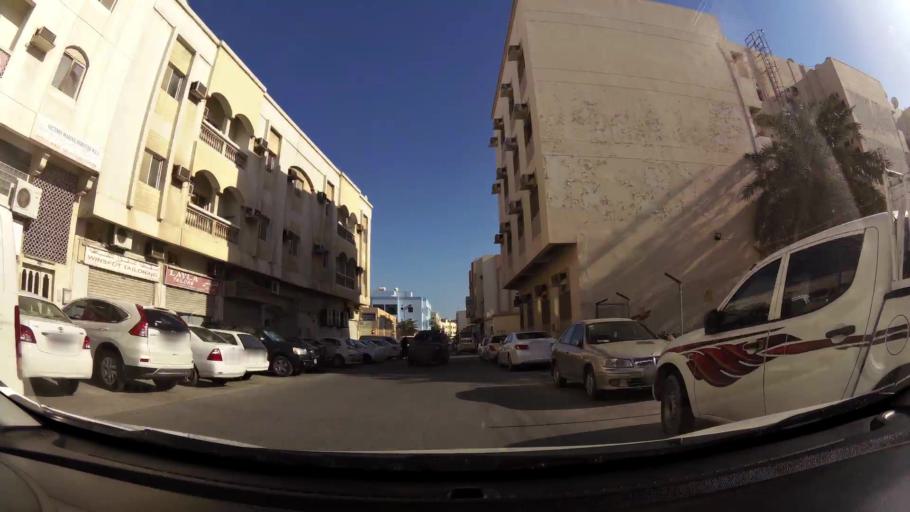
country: BH
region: Manama
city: Manama
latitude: 26.2353
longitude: 50.5844
